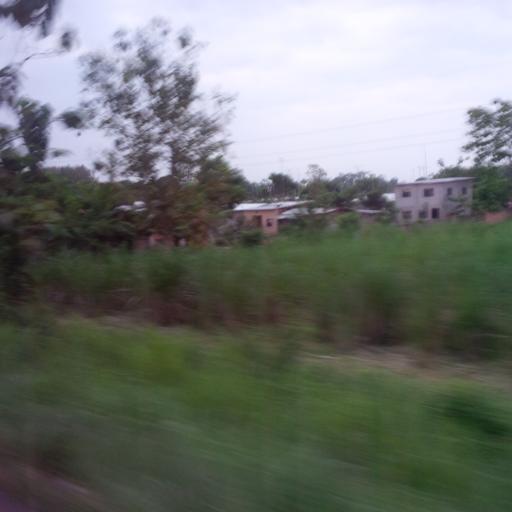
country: EC
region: Canar
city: La Troncal
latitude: -2.3416
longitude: -79.3789
